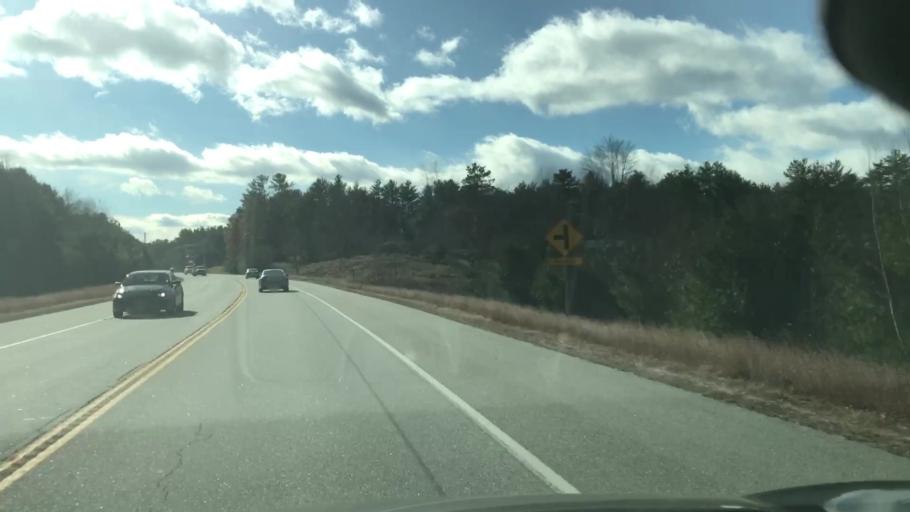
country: US
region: New Hampshire
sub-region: Belknap County
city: Barnstead
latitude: 43.3348
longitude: -71.2997
